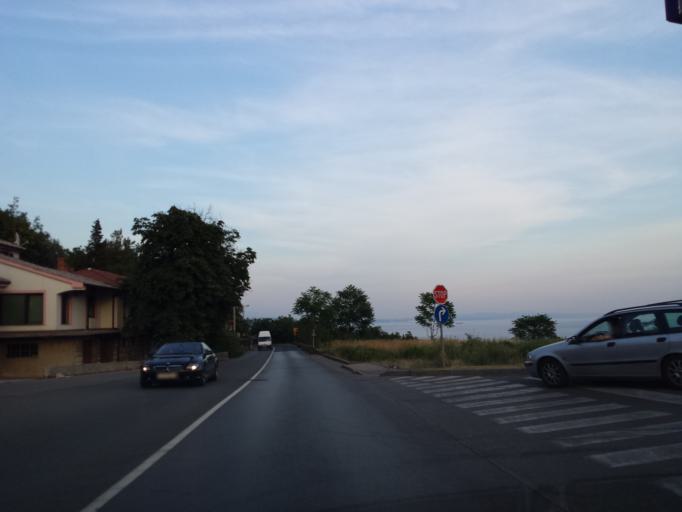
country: HR
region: Primorsko-Goranska
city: Rubesi
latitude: 45.3513
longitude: 14.3666
